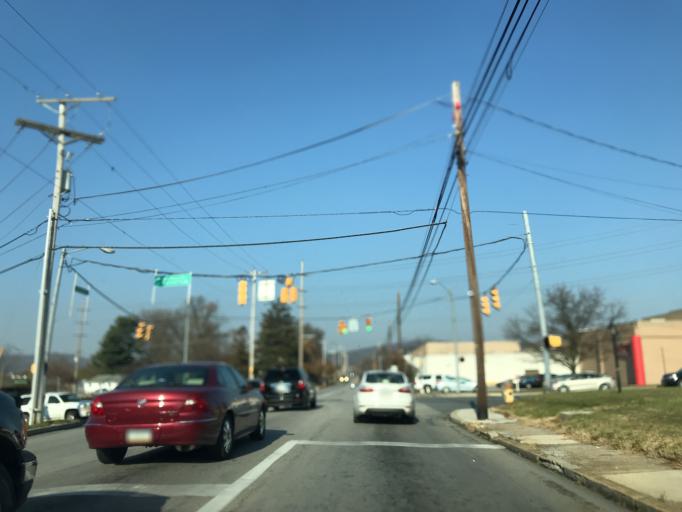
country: US
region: Pennsylvania
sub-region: York County
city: Hanover
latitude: 39.8249
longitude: -76.9727
